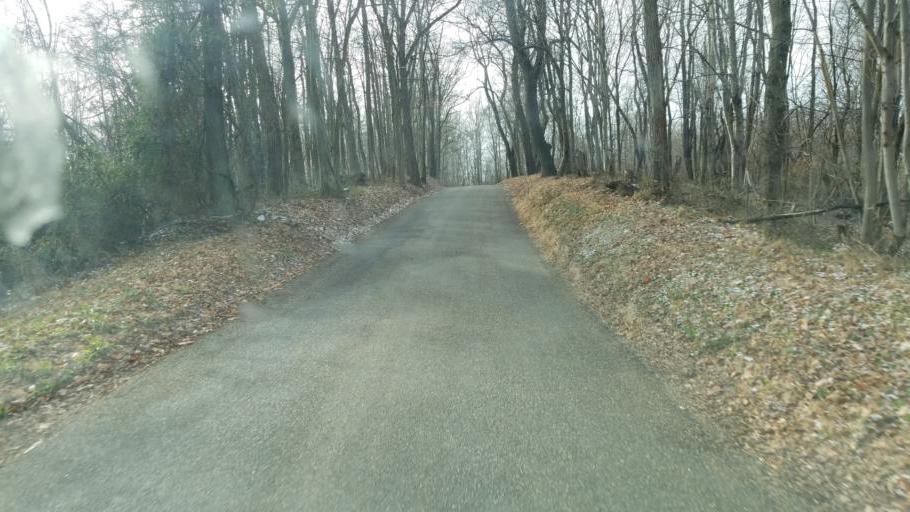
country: US
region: Ohio
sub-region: Muskingum County
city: Dresden
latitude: 40.1290
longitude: -82.0316
